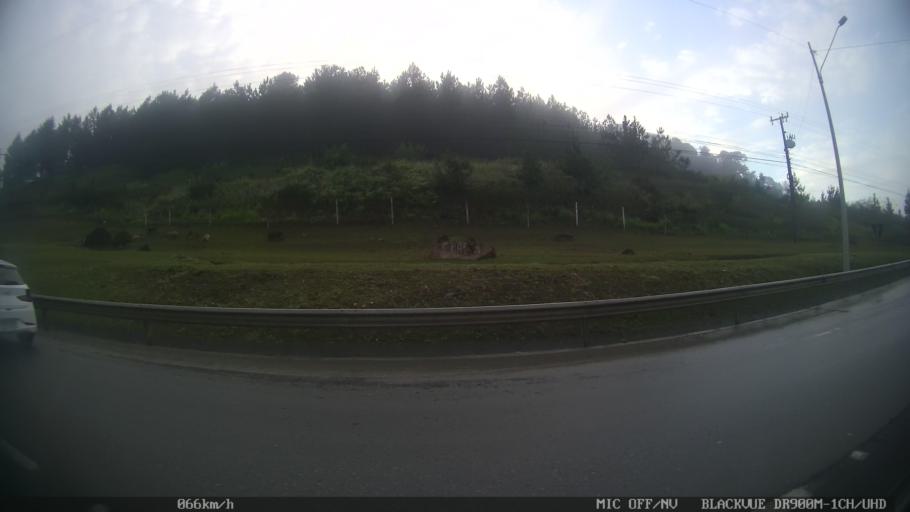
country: BR
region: Santa Catarina
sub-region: Balneario Camboriu
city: Balneario Camboriu
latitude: -26.9900
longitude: -48.6632
